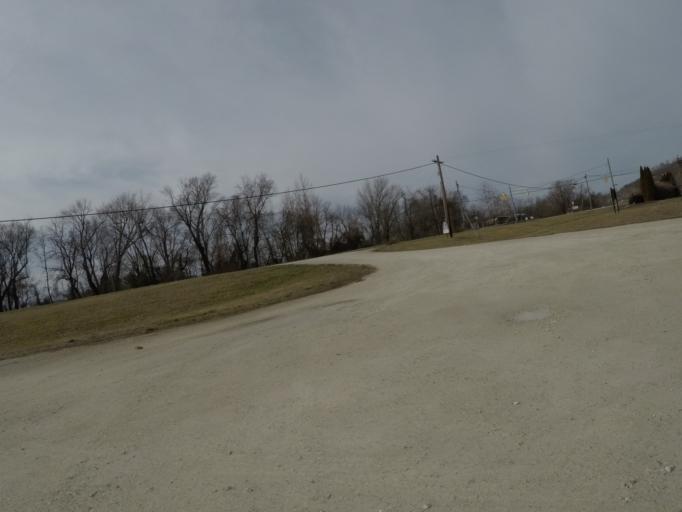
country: US
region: West Virginia
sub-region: Cabell County
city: Pea Ridge
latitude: 38.4431
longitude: -82.3754
